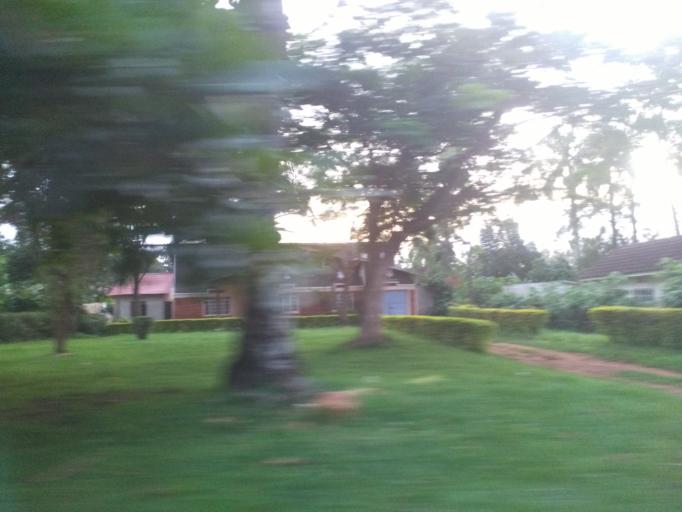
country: UG
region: Eastern Region
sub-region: Jinja District
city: Jinja
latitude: 0.4296
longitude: 33.2017
